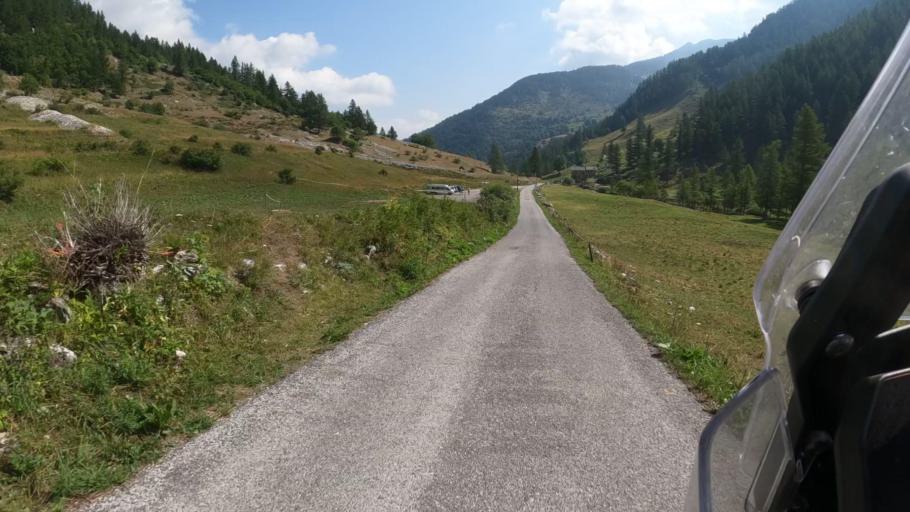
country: IT
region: Piedmont
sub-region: Provincia di Cuneo
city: Canosio
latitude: 44.4203
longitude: 7.0467
